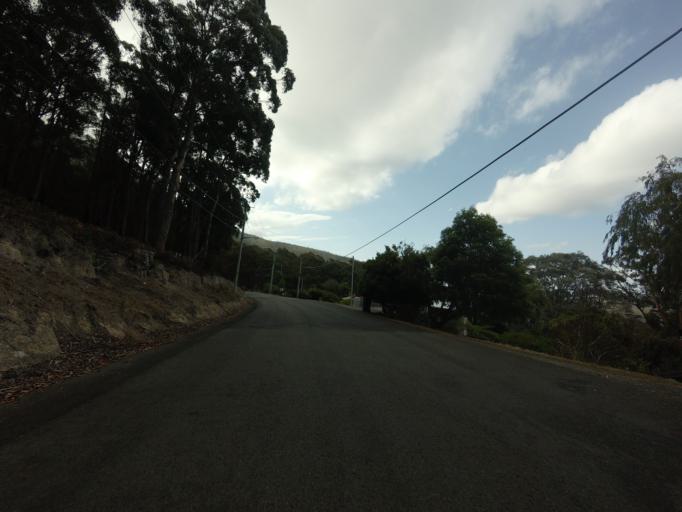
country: AU
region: Tasmania
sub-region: Hobart
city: Dynnyrne
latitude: -42.9089
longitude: 147.2669
